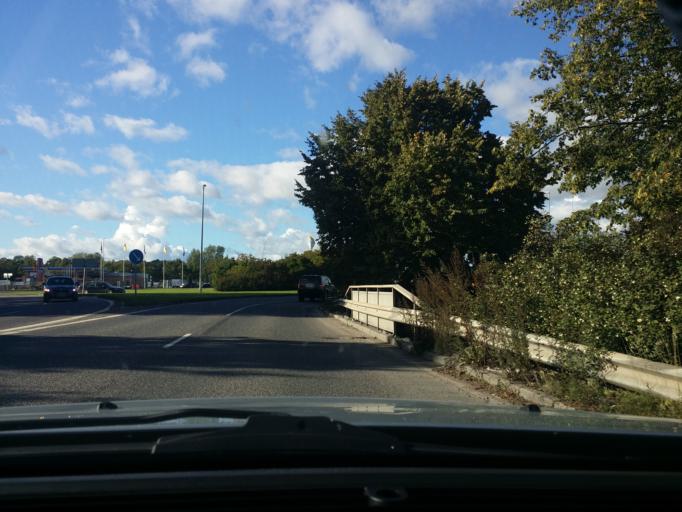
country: SE
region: Vaestmanland
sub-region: Vasteras
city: Vasteras
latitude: 59.6353
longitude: 16.5638
